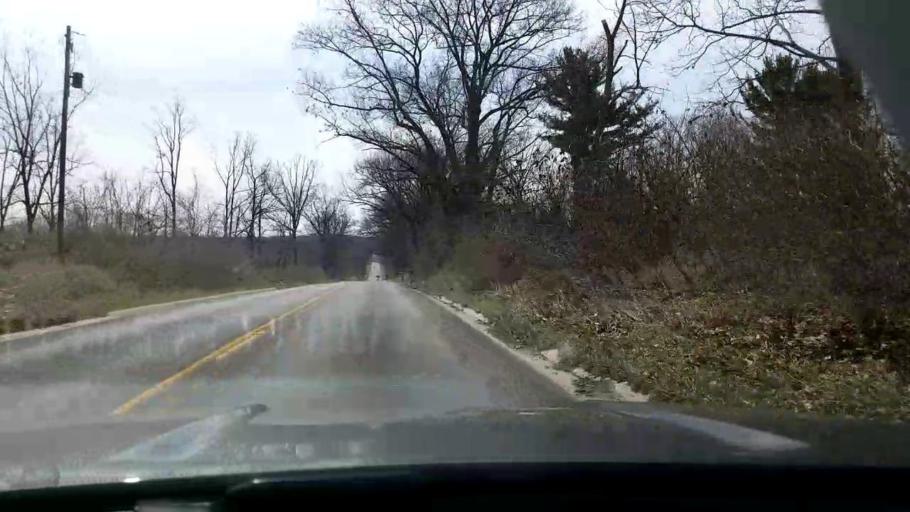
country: US
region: Michigan
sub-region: Jackson County
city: Spring Arbor
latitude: 42.2112
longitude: -84.5213
